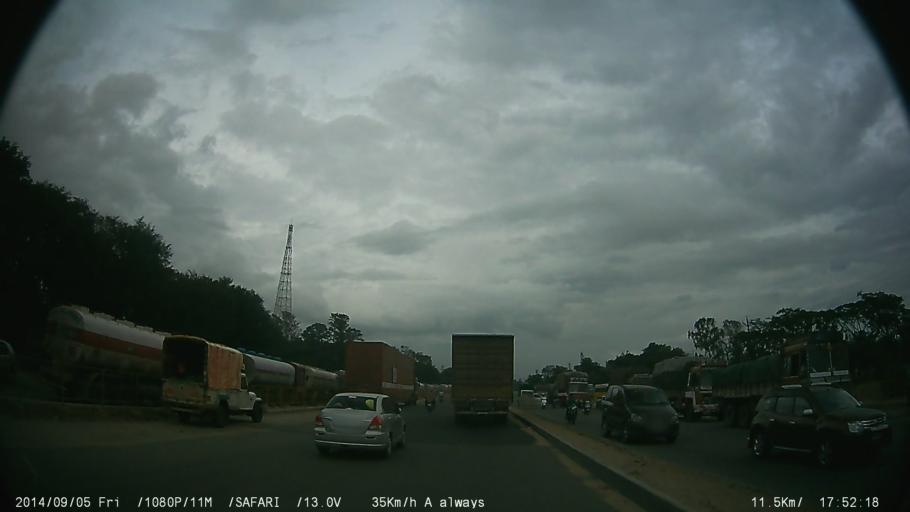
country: IN
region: Tamil Nadu
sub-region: Krishnagiri
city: Hosur
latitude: 12.7619
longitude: 77.7948
